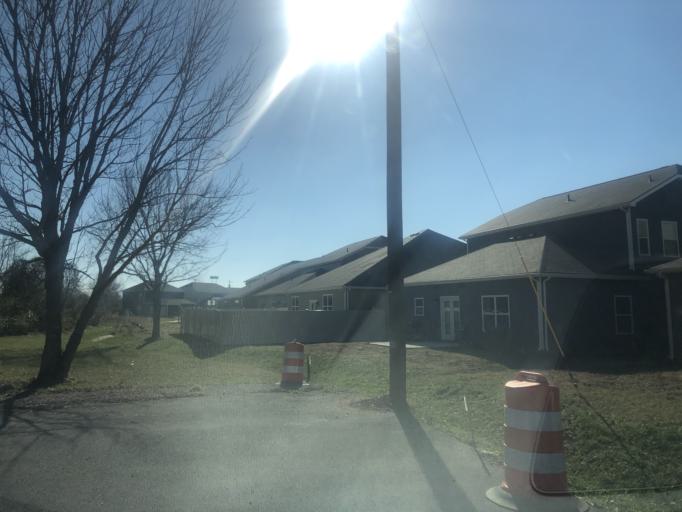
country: US
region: Tennessee
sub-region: Rutherford County
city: Smyrna
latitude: 35.9399
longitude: -86.5319
